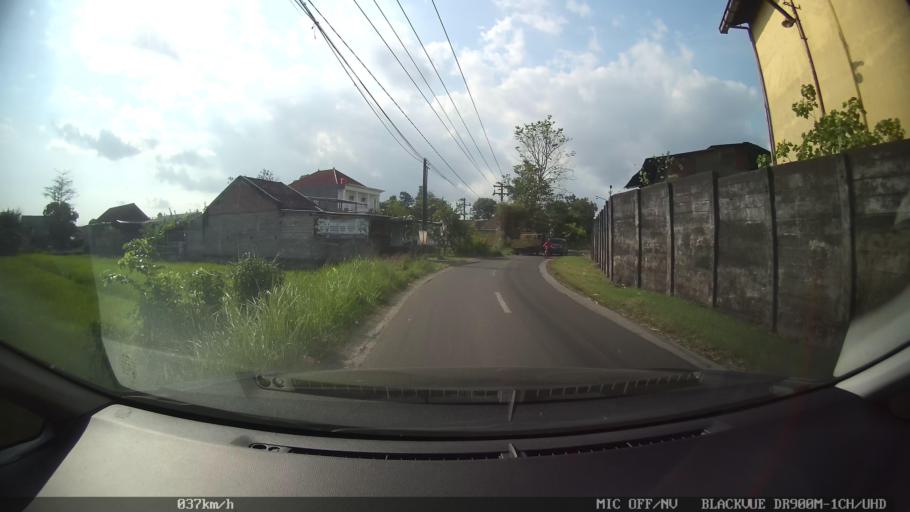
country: ID
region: Daerah Istimewa Yogyakarta
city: Kasihan
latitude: -7.8326
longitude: 110.3447
